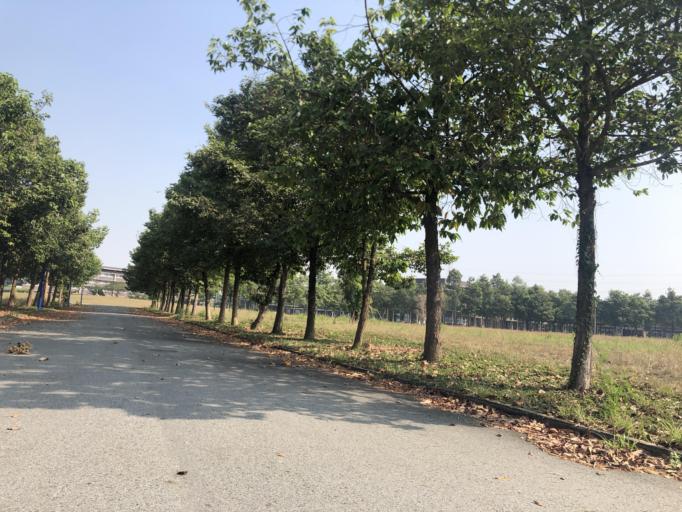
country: VN
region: Binh Duong
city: Thu Dau Mot
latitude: 11.0510
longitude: 106.6656
